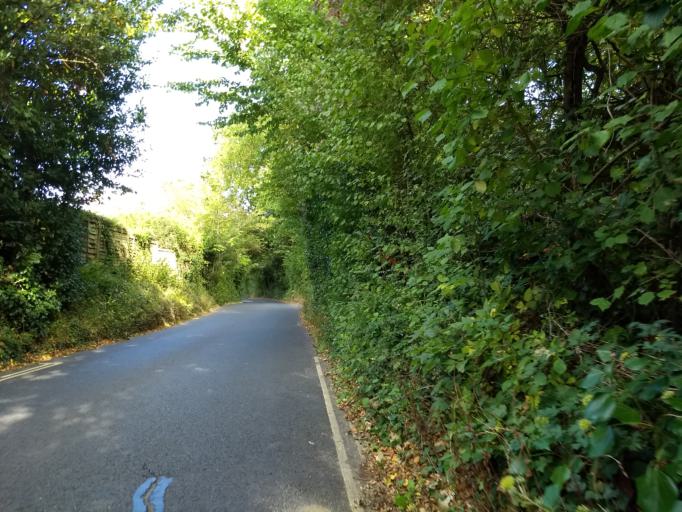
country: GB
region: England
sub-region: Isle of Wight
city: Seaview
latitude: 50.7213
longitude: -1.1241
